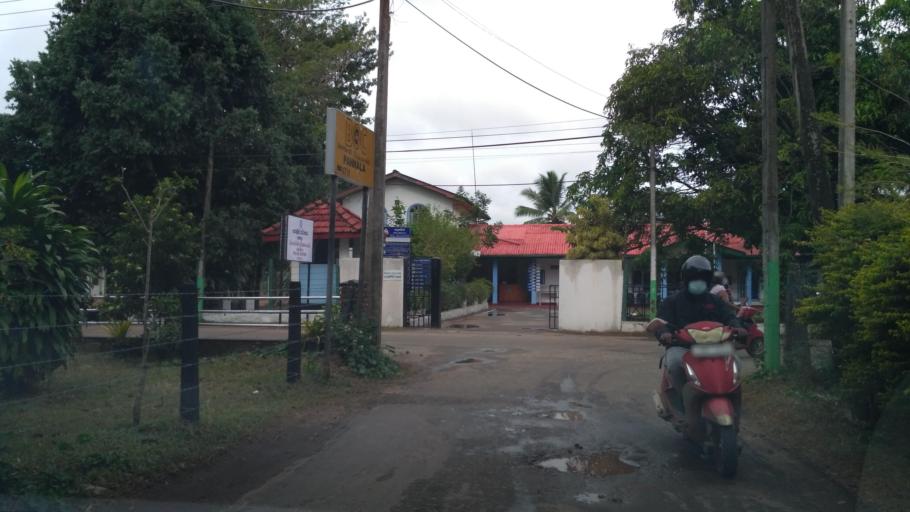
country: LK
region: North Western
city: Kuliyapitiya
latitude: 7.3276
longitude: 80.0220
